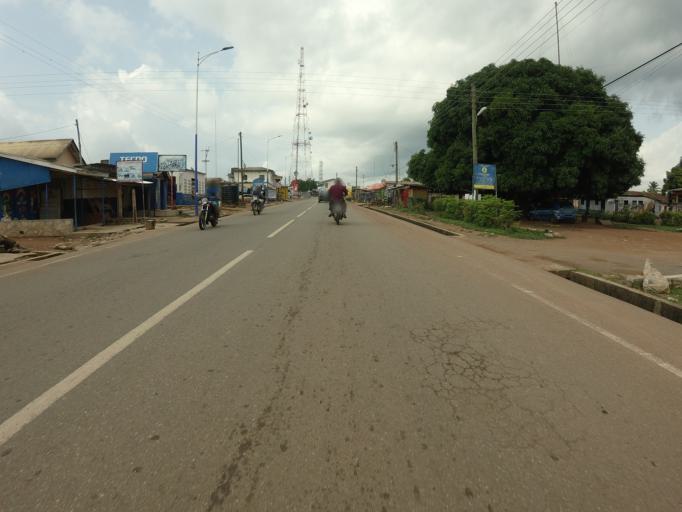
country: GH
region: Volta
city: Hohoe
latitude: 7.1513
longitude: 0.4734
